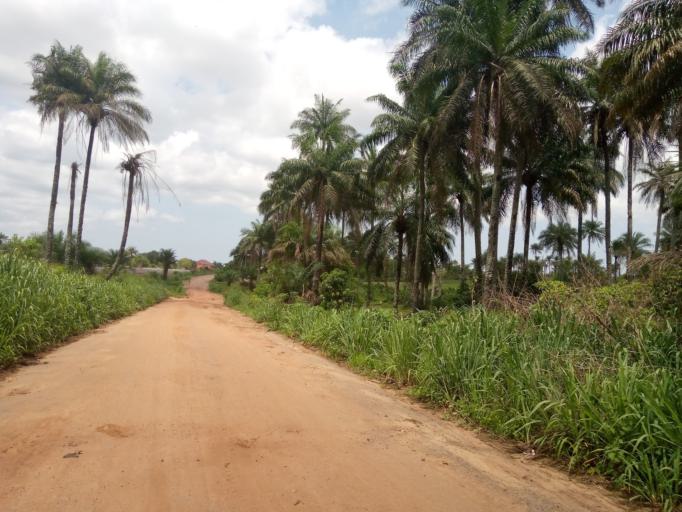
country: SL
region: Western Area
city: Waterloo
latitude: 8.3744
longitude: -12.9594
